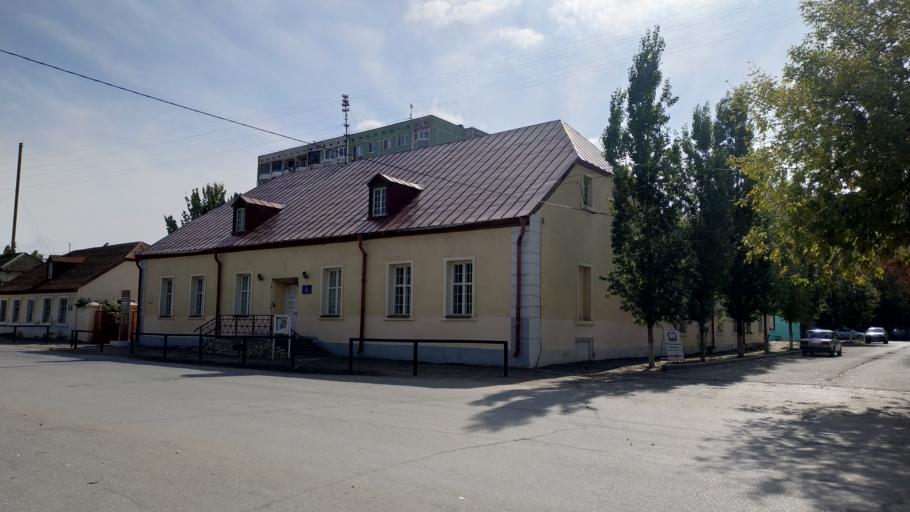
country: RU
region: Volgograd
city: Krasnoslobodsk
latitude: 48.5117
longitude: 44.5496
